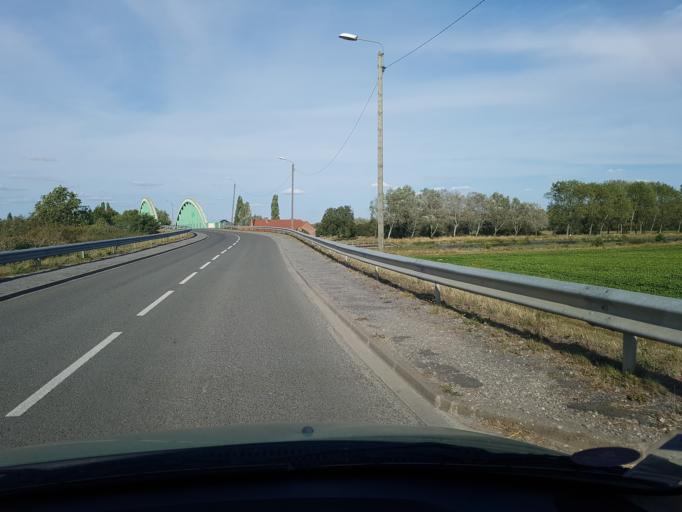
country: FR
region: Nord-Pas-de-Calais
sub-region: Departement du Pas-de-Calais
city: Hinges
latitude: 50.5751
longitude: 2.6237
